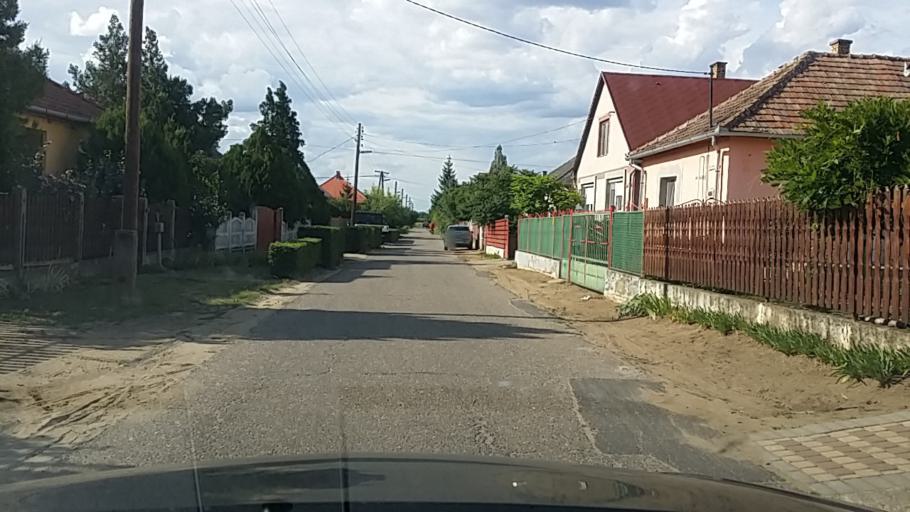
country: HU
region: Szabolcs-Szatmar-Bereg
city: Kek
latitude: 48.1176
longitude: 21.8819
